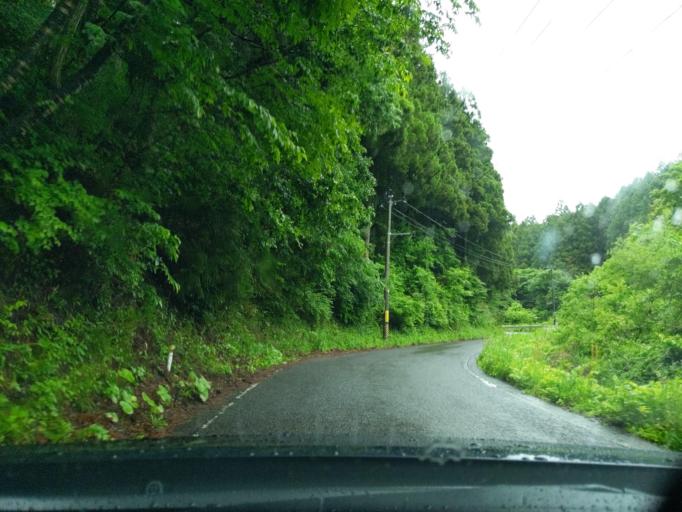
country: JP
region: Fukushima
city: Funehikimachi-funehiki
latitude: 37.5969
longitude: 140.6315
